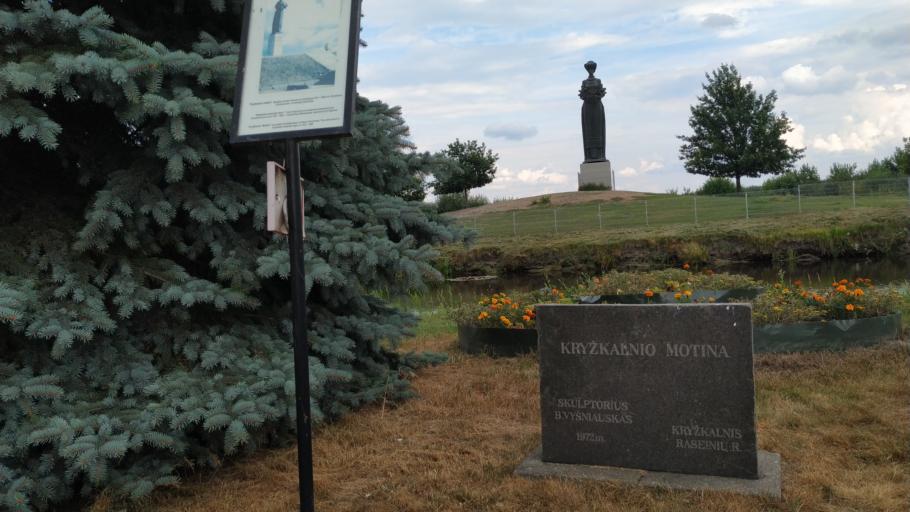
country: LT
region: Alytaus apskritis
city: Druskininkai
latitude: 54.0231
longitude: 24.0794
